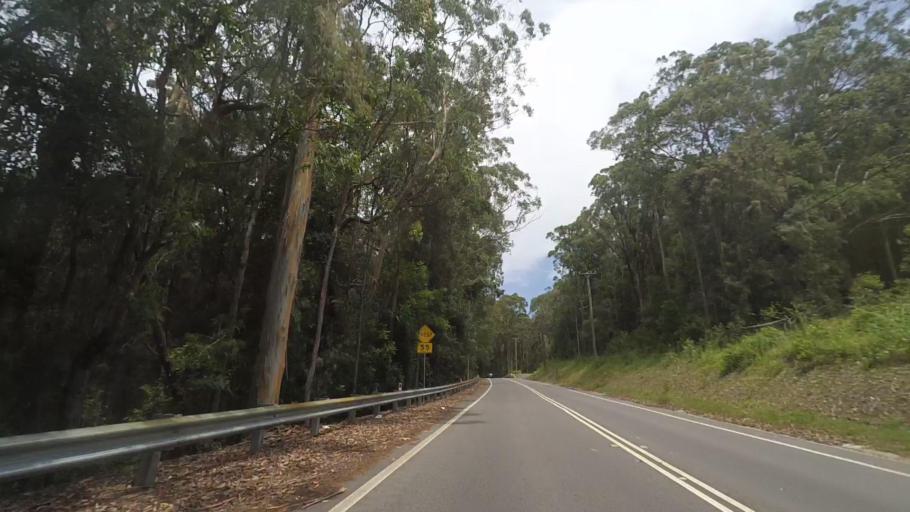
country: AU
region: New South Wales
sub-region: Wyong Shire
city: Chittaway Bay
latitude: -33.3349
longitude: 151.4127
